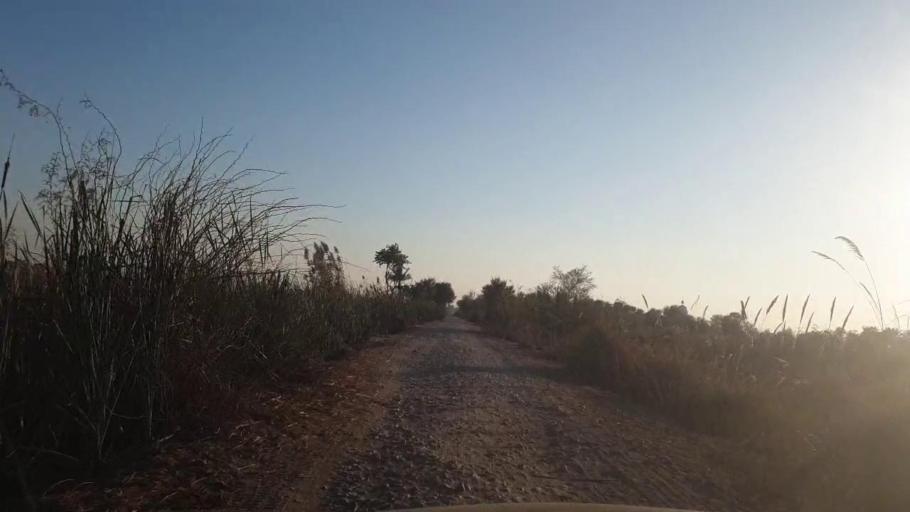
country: PK
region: Sindh
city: Mirpur Mathelo
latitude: 27.9966
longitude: 69.4669
